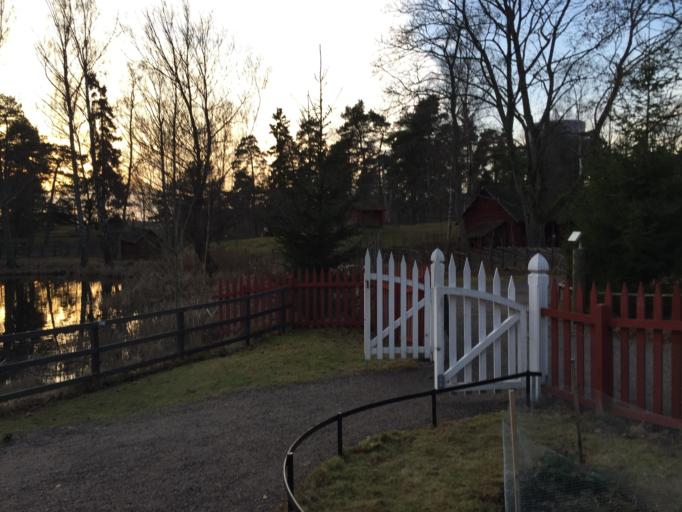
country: SE
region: Stockholm
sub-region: Sodertalje Kommun
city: Soedertaelje
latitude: 59.1918
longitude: 17.6165
